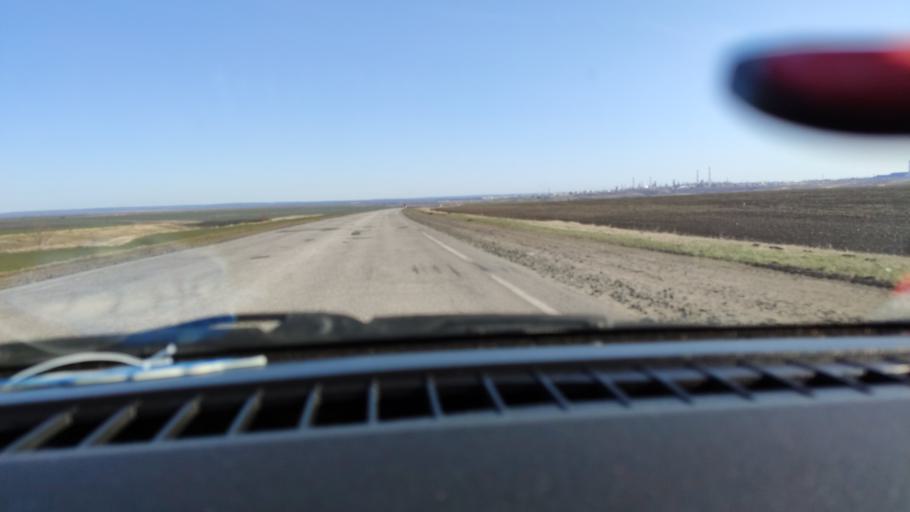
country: RU
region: Samara
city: Varlamovo
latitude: 53.0346
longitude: 48.3361
